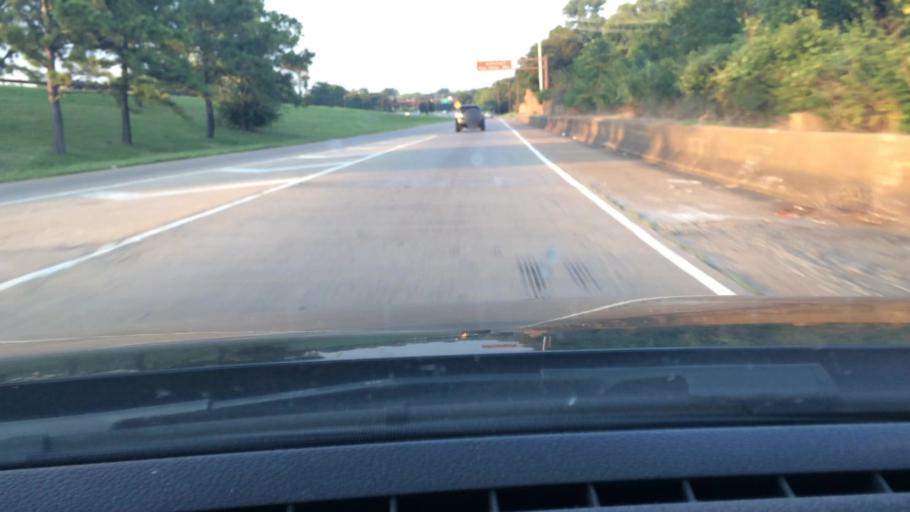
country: US
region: Tennessee
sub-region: Davidson County
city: Oak Hill
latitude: 36.1159
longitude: -86.7709
